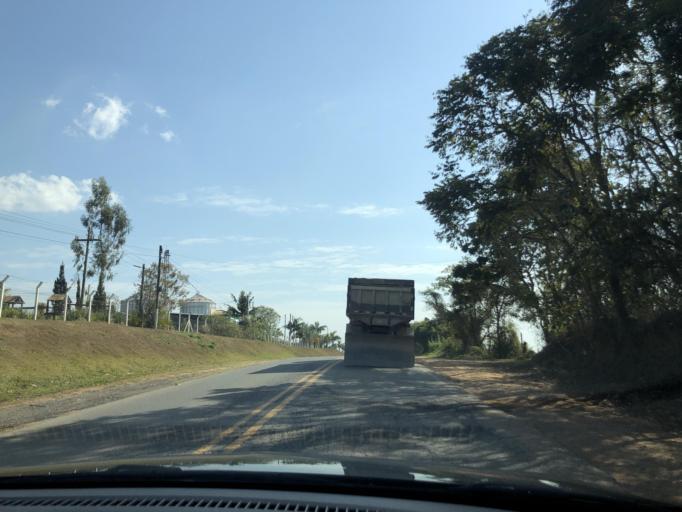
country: BR
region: Sao Paulo
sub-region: Pilar Do Sul
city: Pilar do Sul
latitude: -23.8082
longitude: -47.6985
